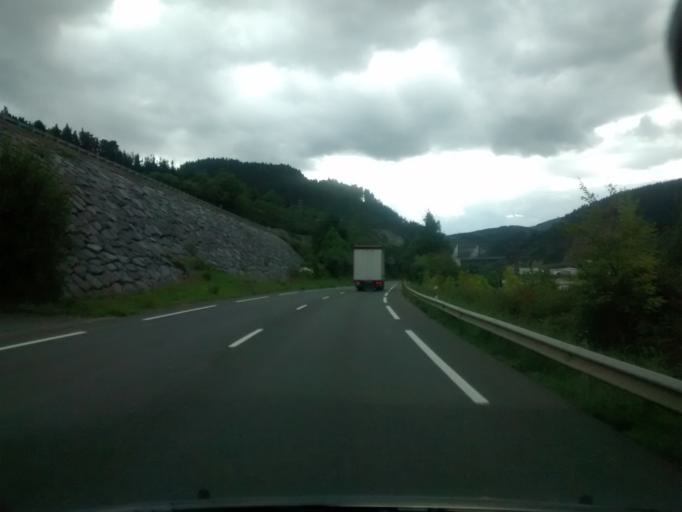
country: ES
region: Basque Country
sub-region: Provincia de Guipuzcoa
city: Arrasate / Mondragon
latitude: 43.0535
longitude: -2.4914
